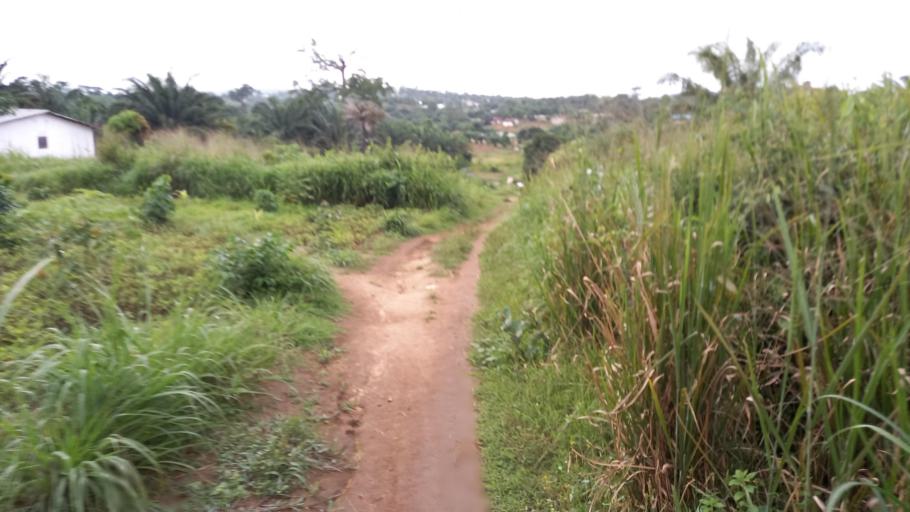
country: SL
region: Eastern Province
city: Kailahun
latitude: 8.2895
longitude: -10.5696
